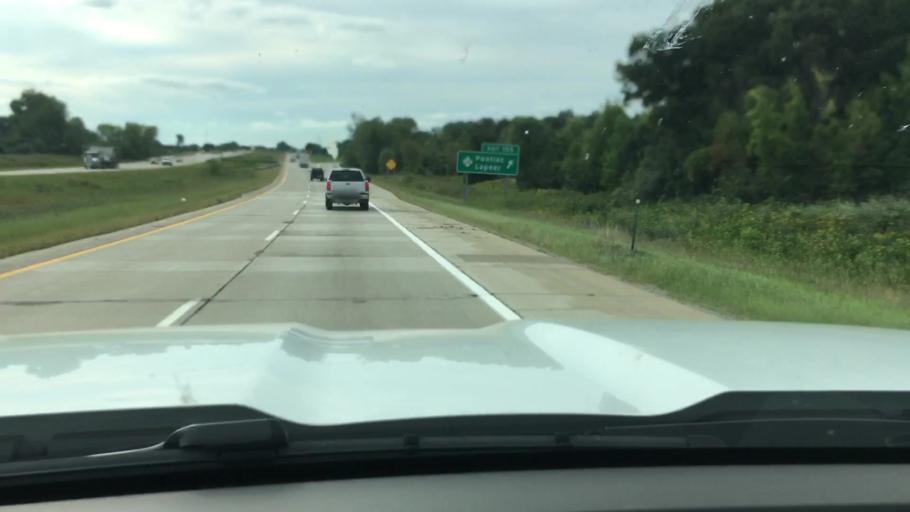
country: US
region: Michigan
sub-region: Lapeer County
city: Lapeer
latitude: 43.0247
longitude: -83.3099
